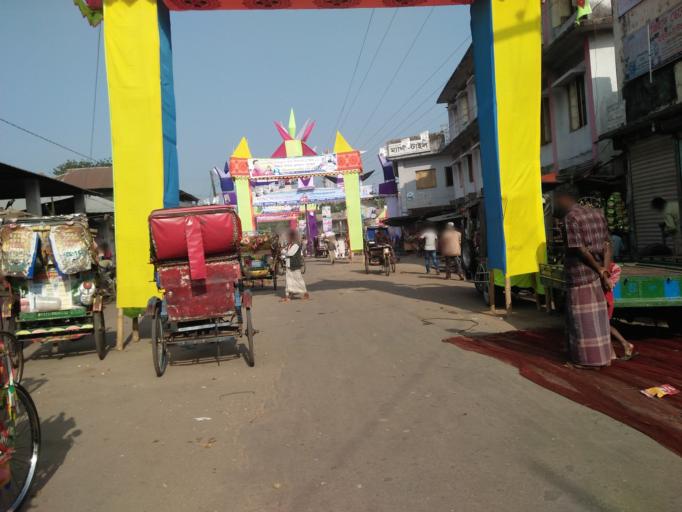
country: BD
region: Khulna
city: Uttar Char Fasson
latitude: 22.1914
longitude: 90.6748
